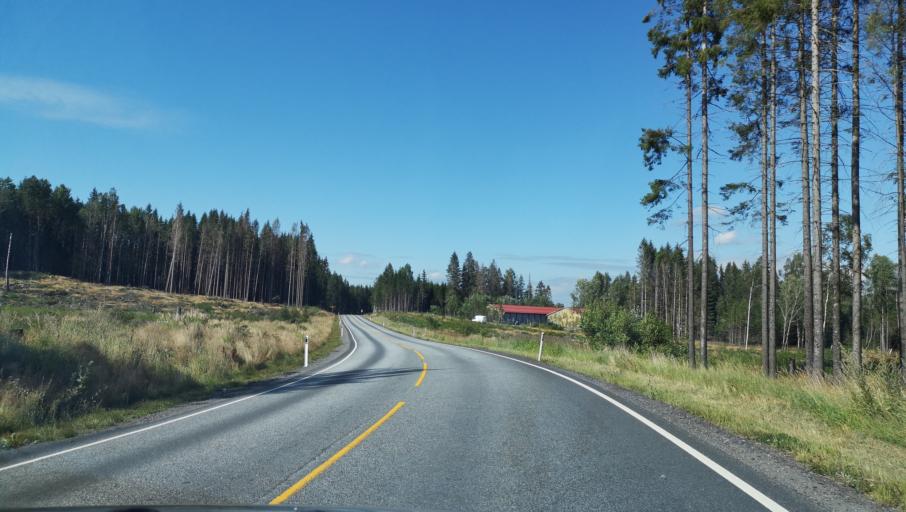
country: NO
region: Ostfold
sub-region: Valer
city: Kirkebygda
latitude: 59.5776
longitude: 10.8756
